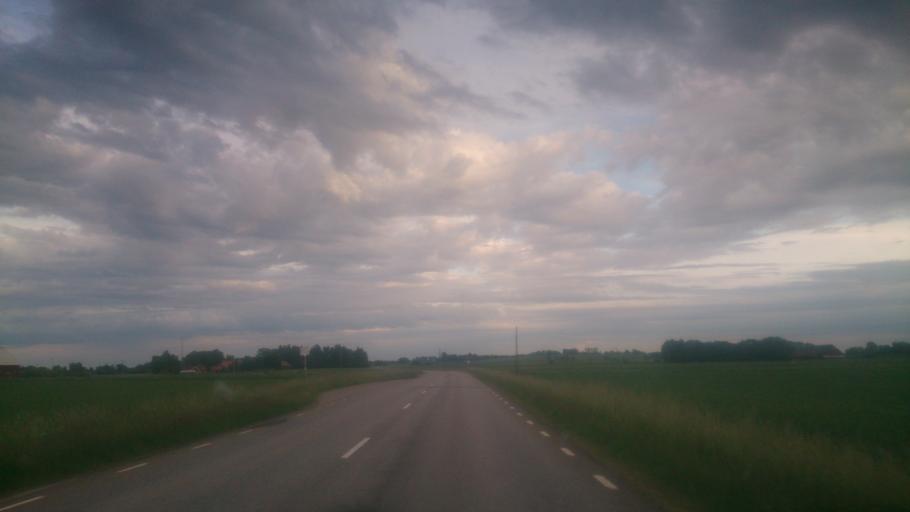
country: SE
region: OEstergoetland
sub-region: Motala Kommun
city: Borensberg
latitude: 58.4892
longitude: 15.2103
